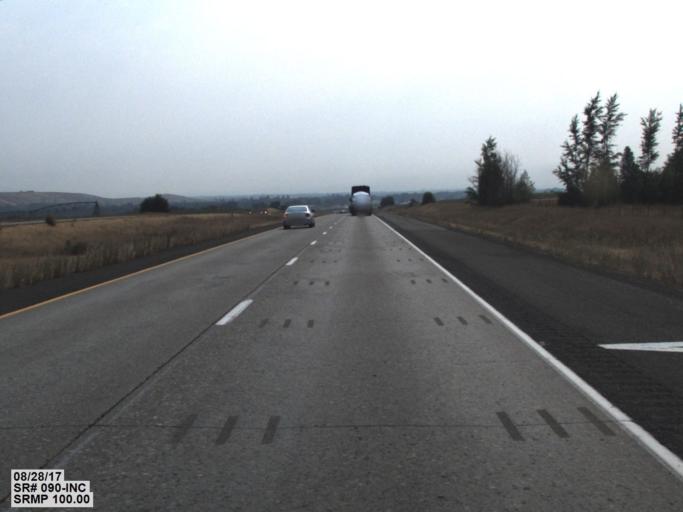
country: US
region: Washington
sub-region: Kittitas County
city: Ellensburg
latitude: 47.0610
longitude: -120.6867
